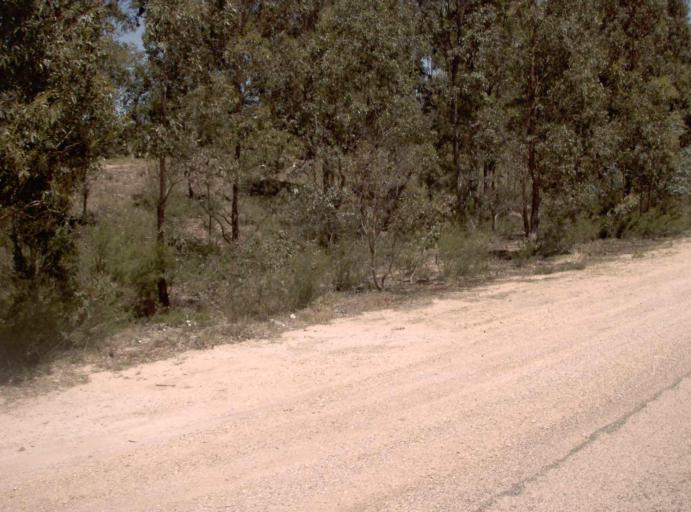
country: AU
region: Victoria
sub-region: East Gippsland
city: Bairnsdale
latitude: -37.7614
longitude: 147.7032
